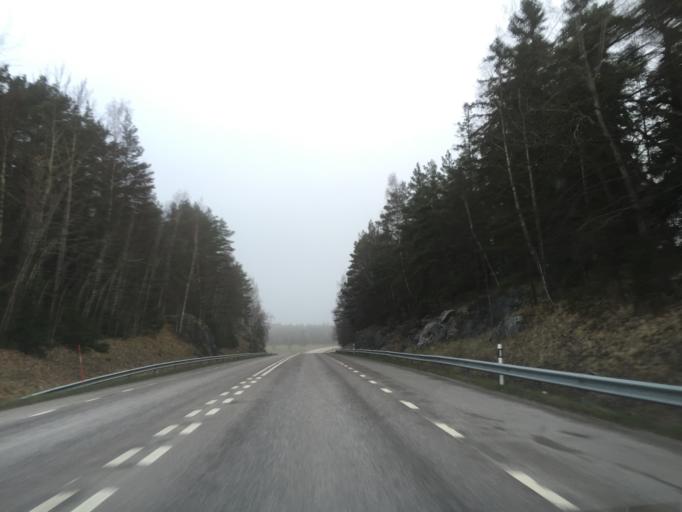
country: SE
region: Soedermanland
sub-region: Nykopings Kommun
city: Stigtomta
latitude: 58.8216
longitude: 16.7596
